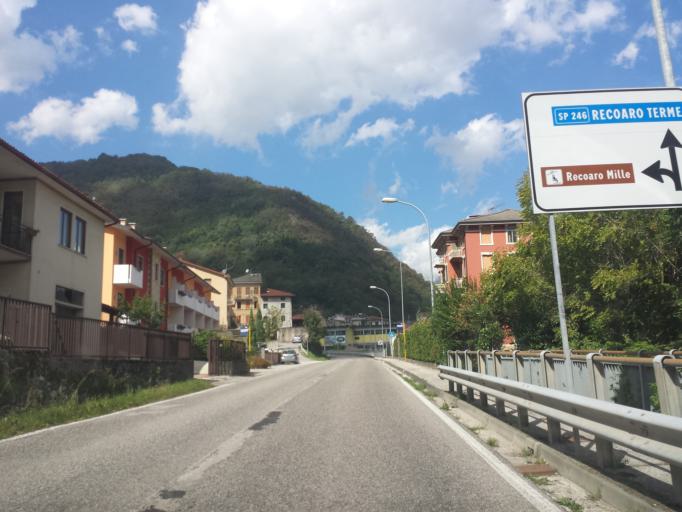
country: IT
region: Veneto
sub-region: Provincia di Vicenza
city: San Quirico
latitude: 45.6734
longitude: 11.2736
